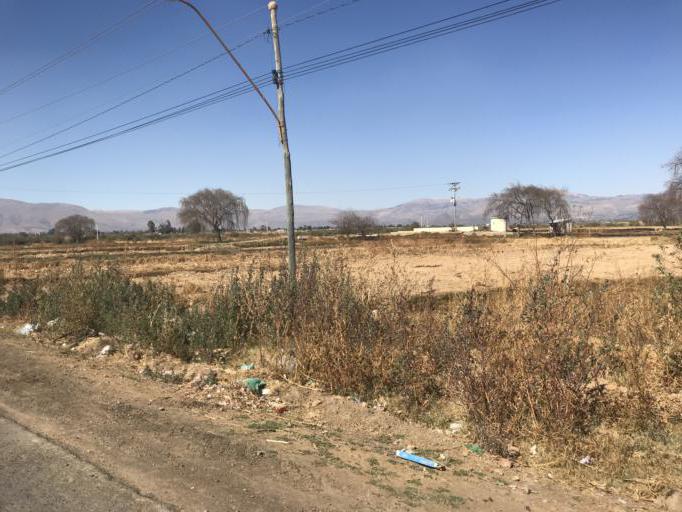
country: BO
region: Cochabamba
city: Cliza
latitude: -17.5714
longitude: -65.8976
